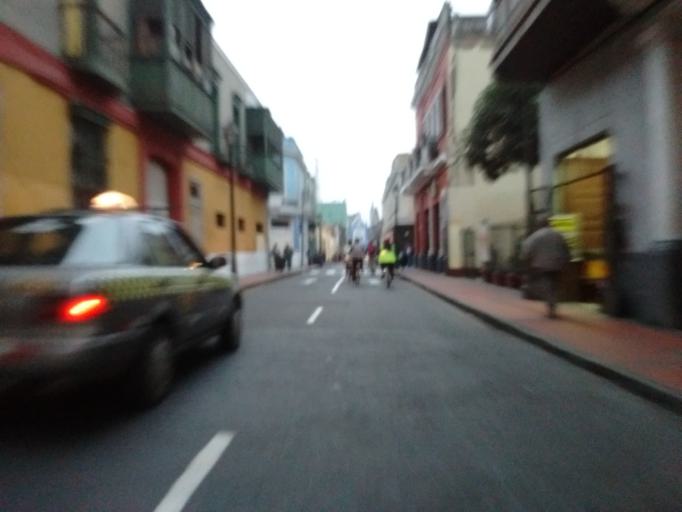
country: PE
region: Lima
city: Lima
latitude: -12.0510
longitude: -77.0362
